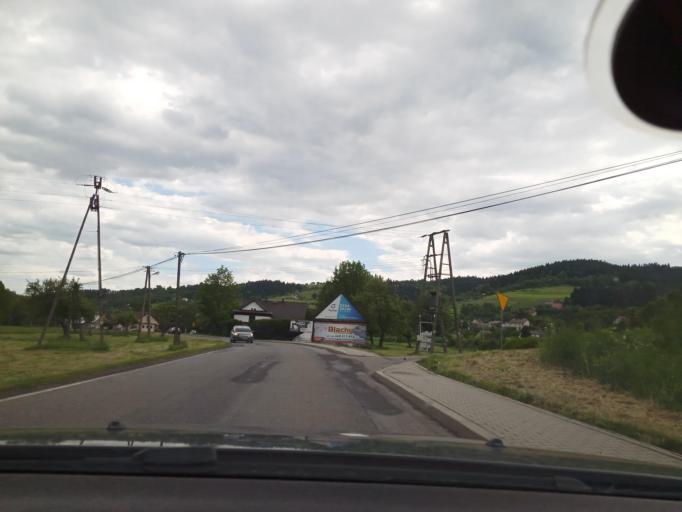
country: PL
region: Lesser Poland Voivodeship
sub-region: Powiat limanowski
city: Tymbark
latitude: 49.7435
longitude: 20.3689
